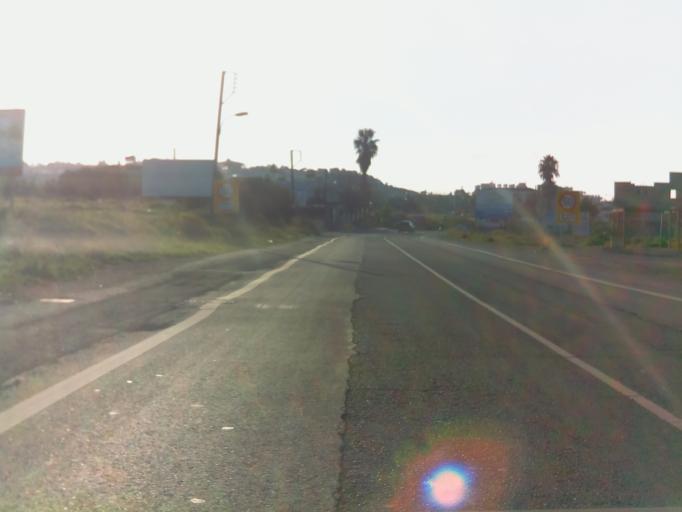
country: CY
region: Pafos
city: Chlorakas
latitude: 34.7882
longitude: 32.4039
